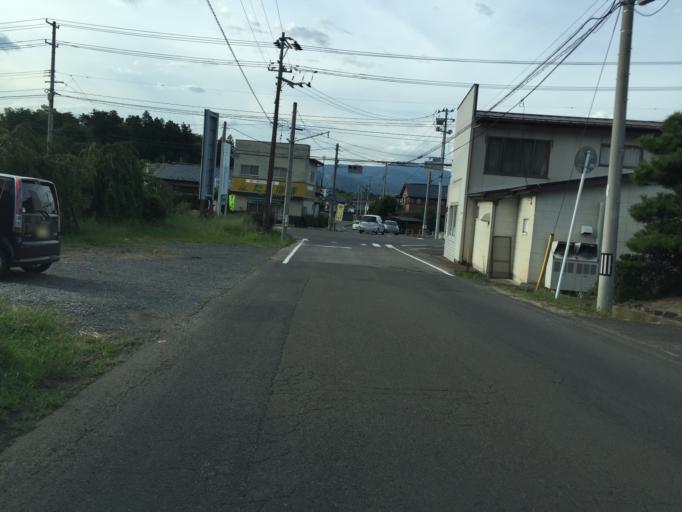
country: JP
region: Fukushima
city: Hobaramachi
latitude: 37.8045
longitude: 140.5268
